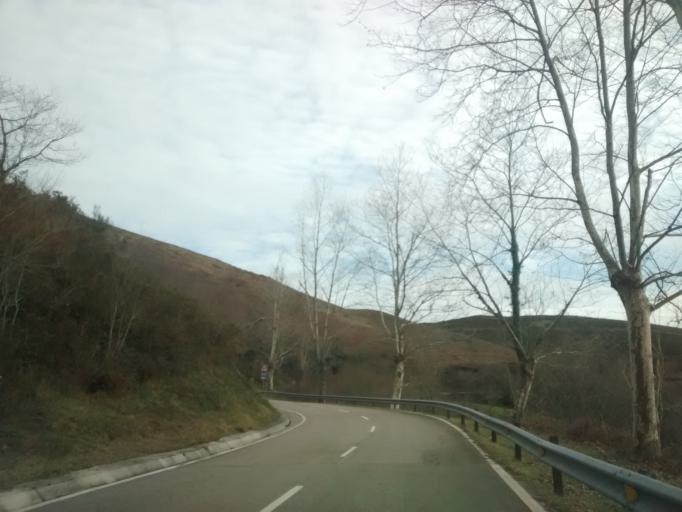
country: ES
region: Cantabria
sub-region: Provincia de Cantabria
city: Ruente
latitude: 43.2471
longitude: -4.3264
